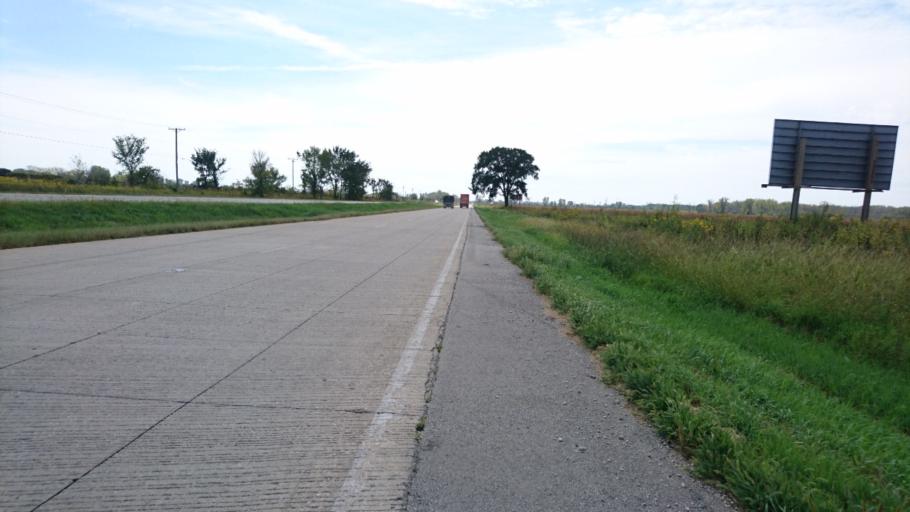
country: US
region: Illinois
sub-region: Will County
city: Wilmington
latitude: 41.3490
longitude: -88.1337
